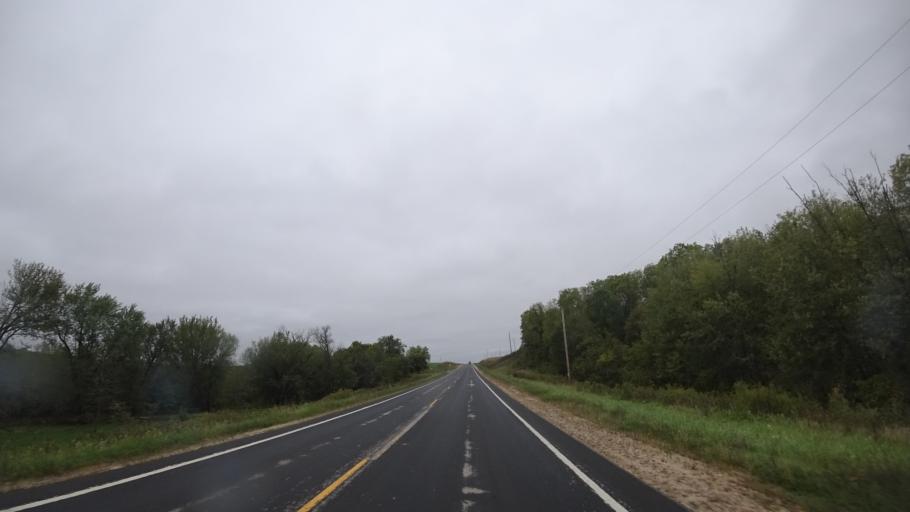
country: US
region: Wisconsin
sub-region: Grant County
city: Boscobel
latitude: 43.1096
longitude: -90.8054
